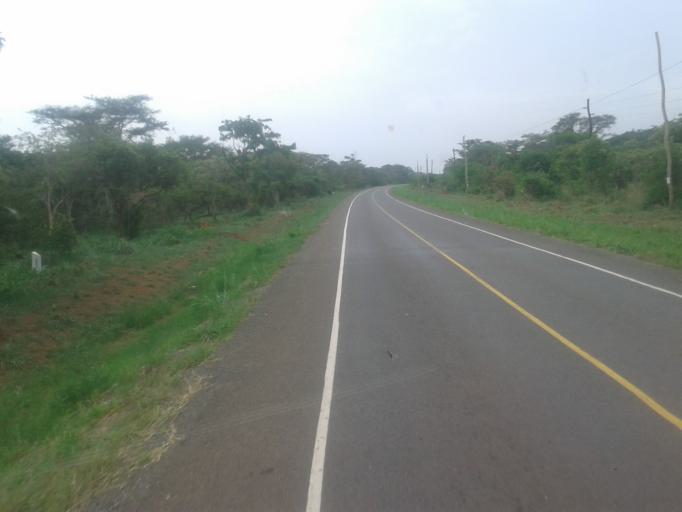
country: UG
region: Northern Region
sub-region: Oyam District
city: Oyam
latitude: 2.2549
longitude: 32.2426
